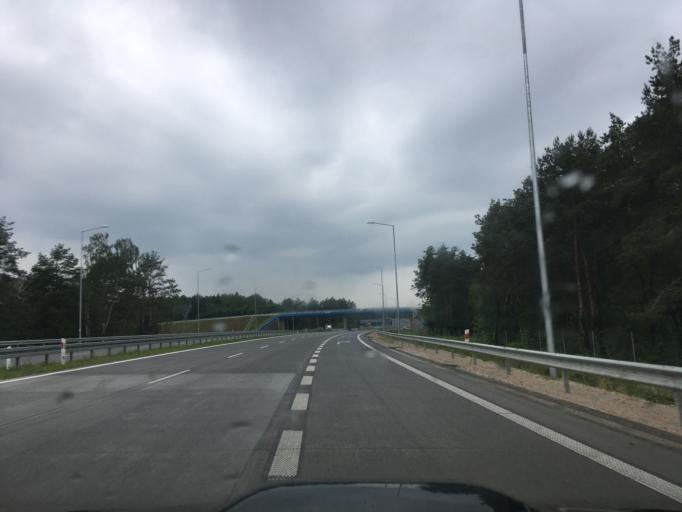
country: PL
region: Masovian Voivodeship
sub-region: Powiat piaseczynski
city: Gora Kalwaria
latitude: 51.9695
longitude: 21.2055
